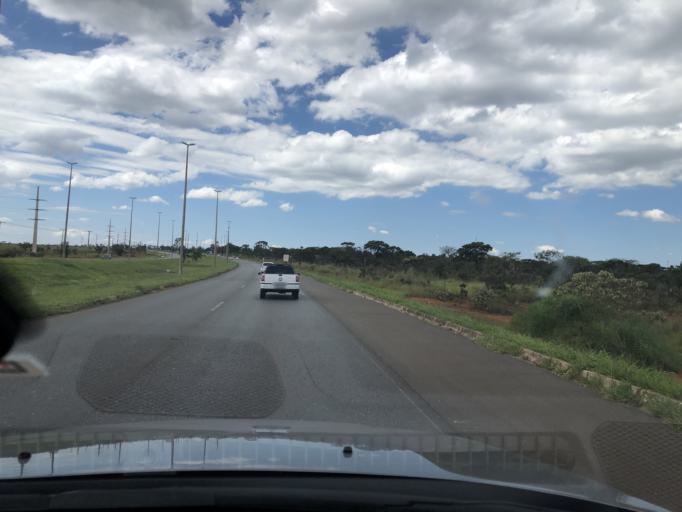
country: BR
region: Federal District
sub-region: Brasilia
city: Brasilia
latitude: -15.9778
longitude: -48.0051
